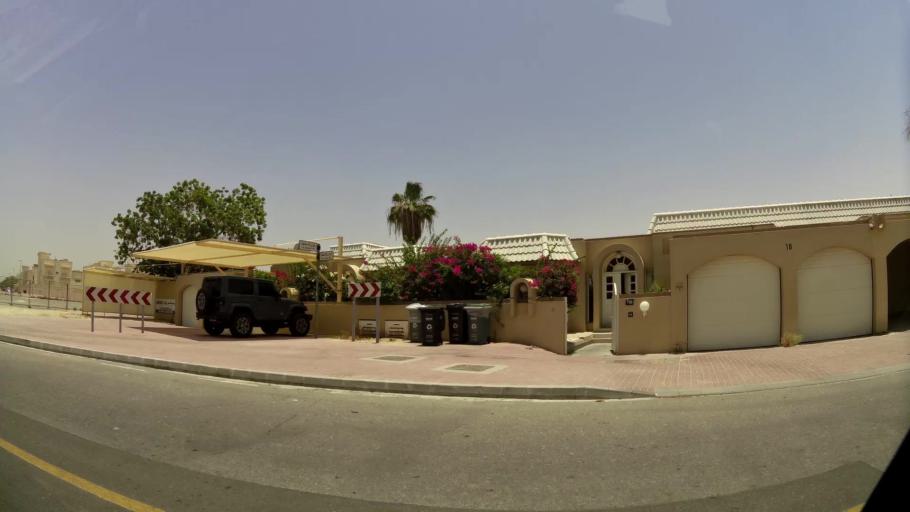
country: AE
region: Dubai
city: Dubai
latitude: 25.1725
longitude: 55.2286
